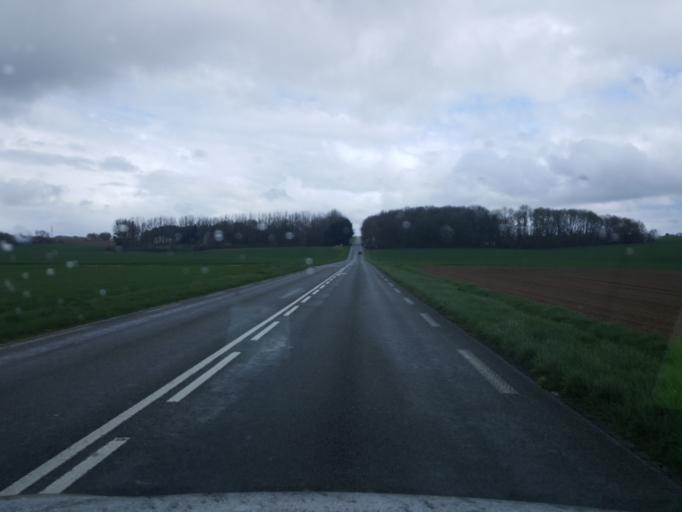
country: FR
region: Picardie
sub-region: Departement de l'Oise
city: Chaumont-en-Vexin
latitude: 49.3003
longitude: 1.8615
